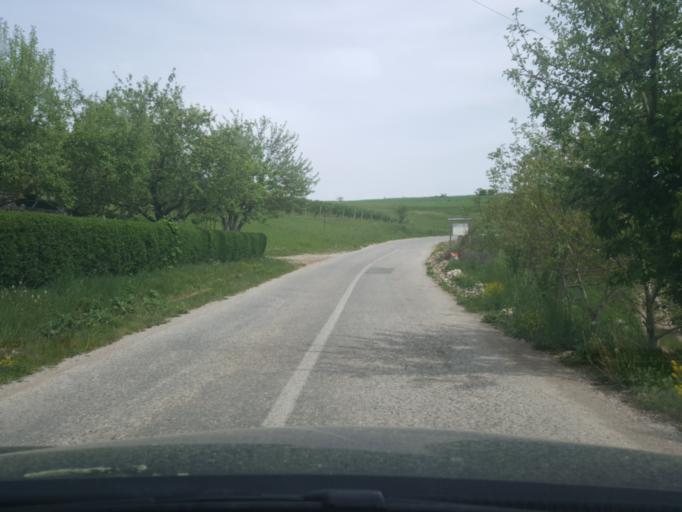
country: RS
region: Central Serbia
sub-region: Zlatiborski Okrug
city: Bajina Basta
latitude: 43.9002
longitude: 19.5132
